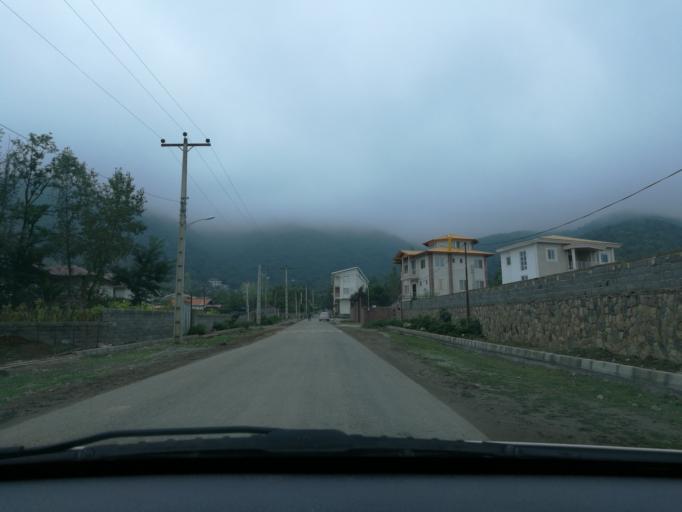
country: IR
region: Mazandaran
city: `Abbasabad
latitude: 36.4989
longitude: 51.2158
